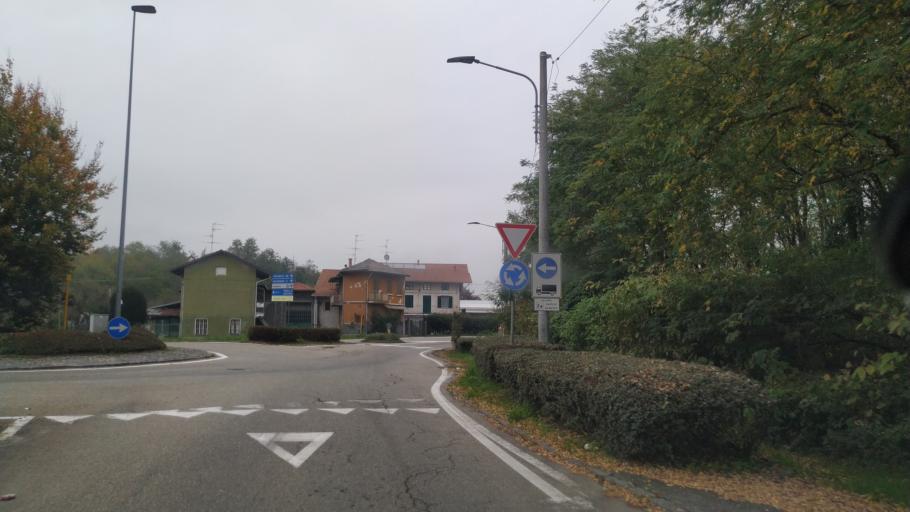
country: IT
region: Piedmont
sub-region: Provincia di Biella
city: Cerreto Castello
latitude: 45.5586
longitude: 8.1715
